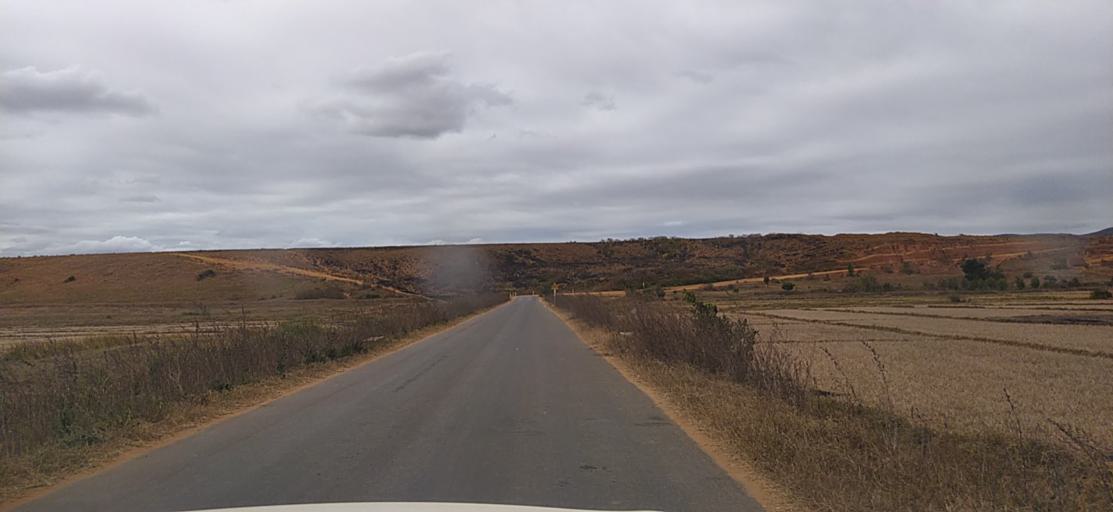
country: MG
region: Alaotra Mangoro
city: Ambatondrazaka
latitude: -17.9136
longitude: 48.2602
